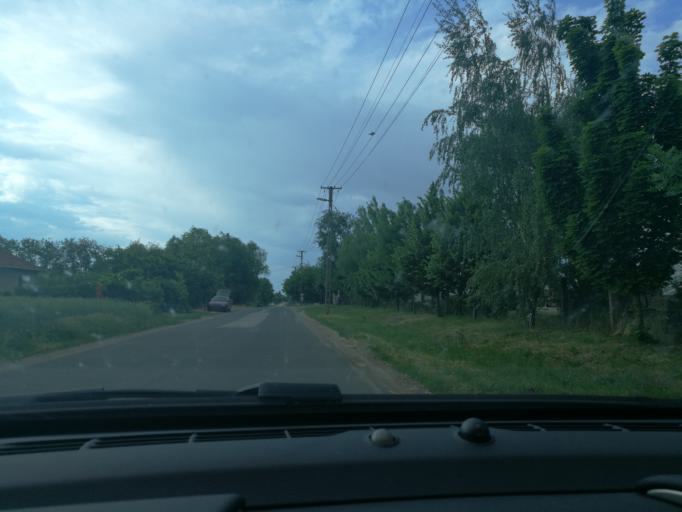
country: HU
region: Szabolcs-Szatmar-Bereg
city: Nyirpazony
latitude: 47.9361
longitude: 21.7965
